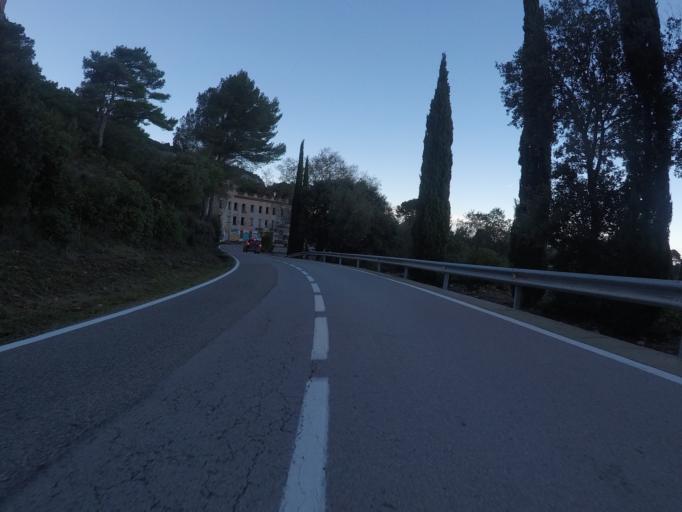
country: ES
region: Catalonia
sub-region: Provincia de Barcelona
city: Monistrol de Montserrat
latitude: 41.6077
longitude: 1.8263
